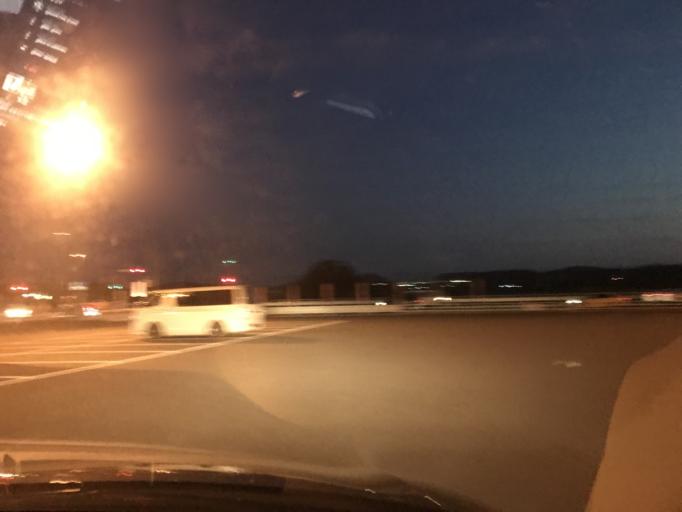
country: JP
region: Chiba
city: Katori-shi
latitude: 35.8959
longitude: 140.5060
